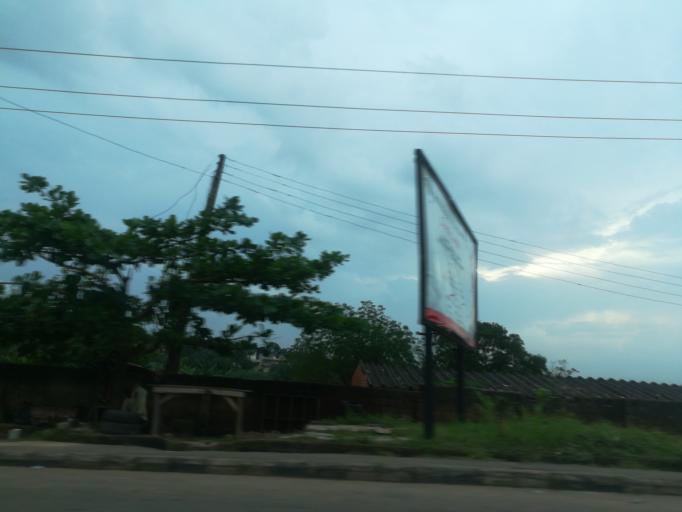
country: NG
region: Oyo
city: Ibadan
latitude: 7.4365
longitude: 3.9075
